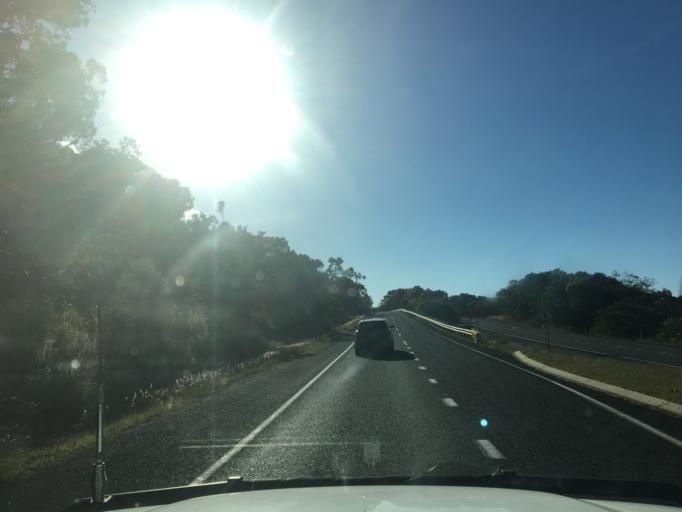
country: AU
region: Queensland
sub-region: Cairns
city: Palm Cove
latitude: -16.7030
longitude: 145.6239
